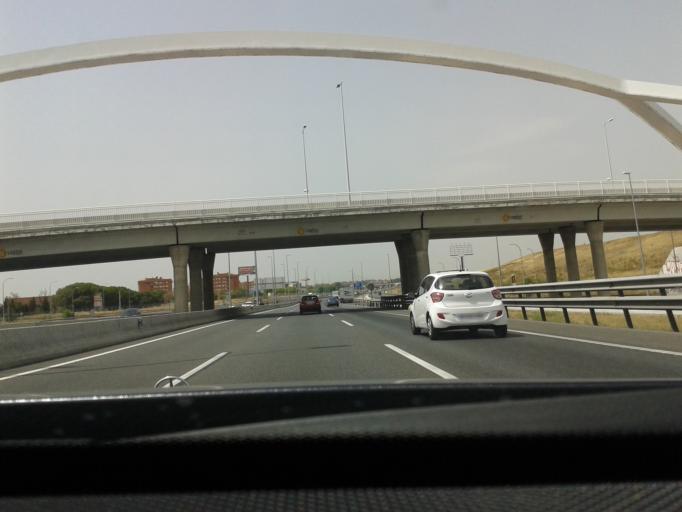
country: ES
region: Madrid
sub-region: Provincia de Madrid
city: Torrejon de Ardoz
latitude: 40.4682
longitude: -3.4390
